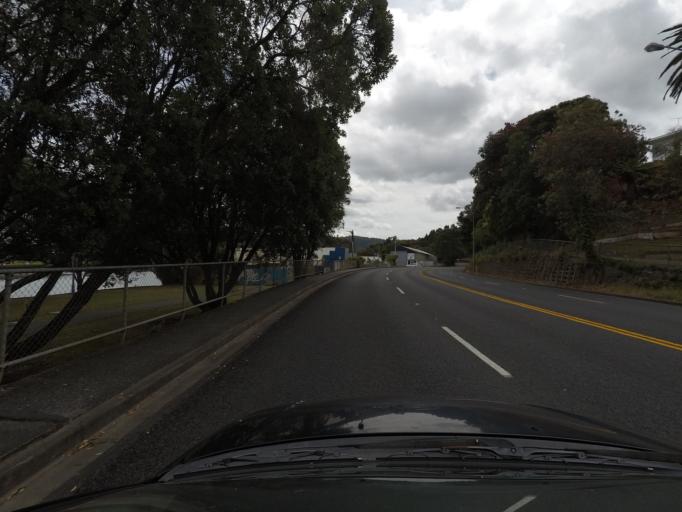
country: NZ
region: Northland
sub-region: Whangarei
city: Whangarei
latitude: -35.7266
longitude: 174.3326
